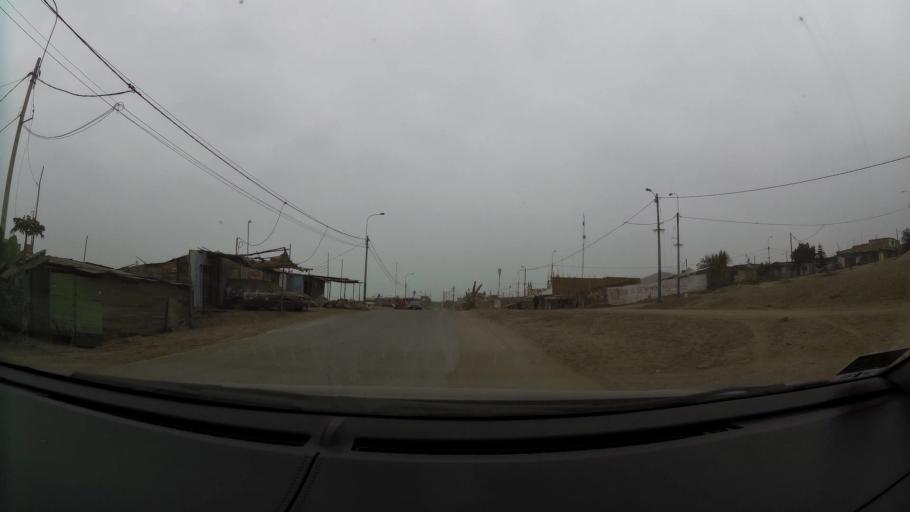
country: PE
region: Lima
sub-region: Lima
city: Santa Rosa
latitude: -11.8382
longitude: -77.1572
